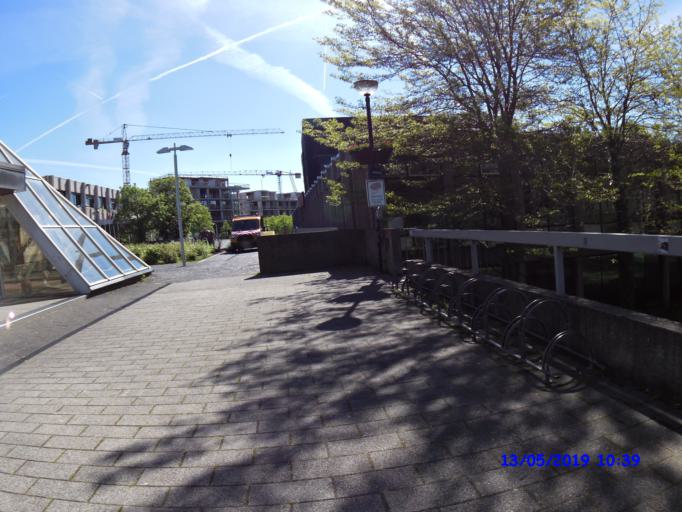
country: BE
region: Flanders
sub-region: Provincie West-Vlaanderen
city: Waregem
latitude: 50.8848
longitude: 3.4317
